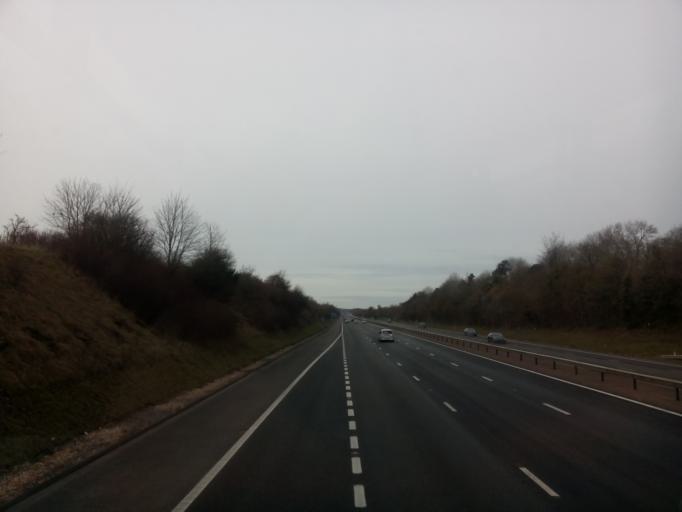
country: GB
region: England
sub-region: Hampshire
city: Basingstoke
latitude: 51.2549
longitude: -1.0719
